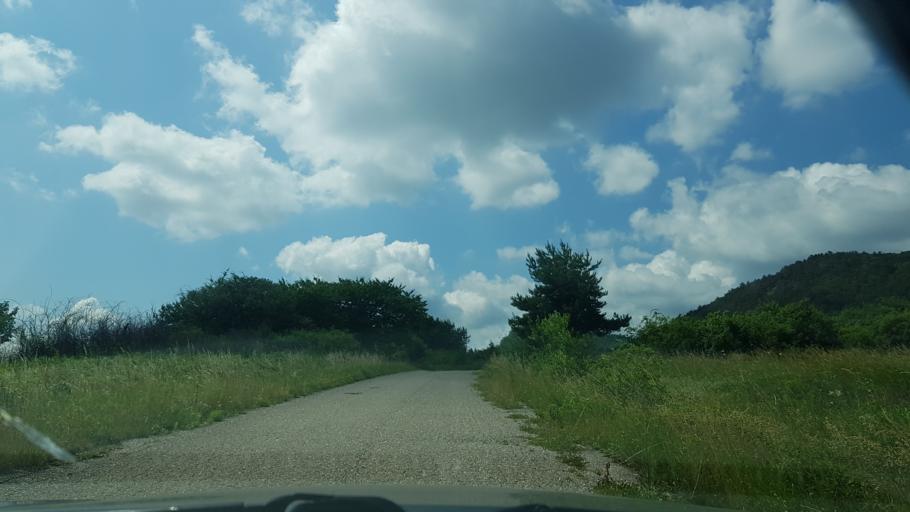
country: HU
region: Borsod-Abauj-Zemplen
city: Gonc
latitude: 48.5344
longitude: 21.4745
